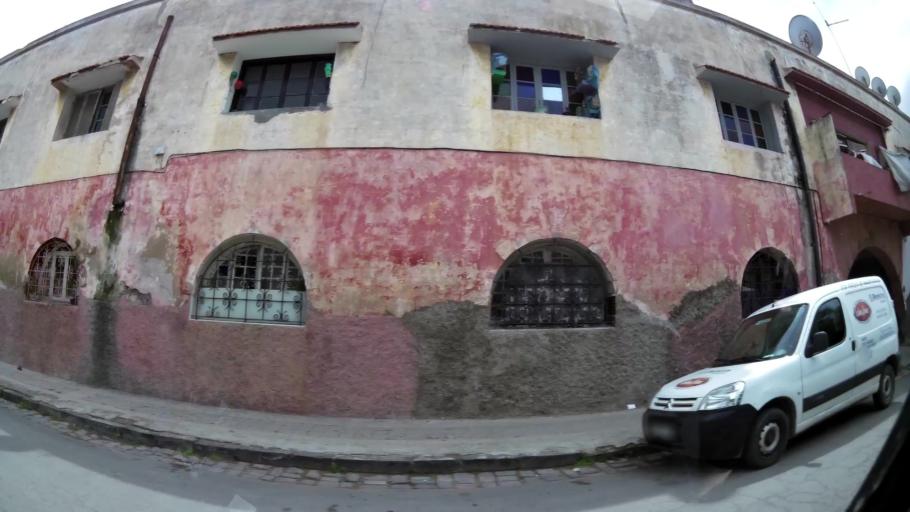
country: MA
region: Grand Casablanca
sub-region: Casablanca
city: Casablanca
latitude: 33.6070
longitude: -7.5482
